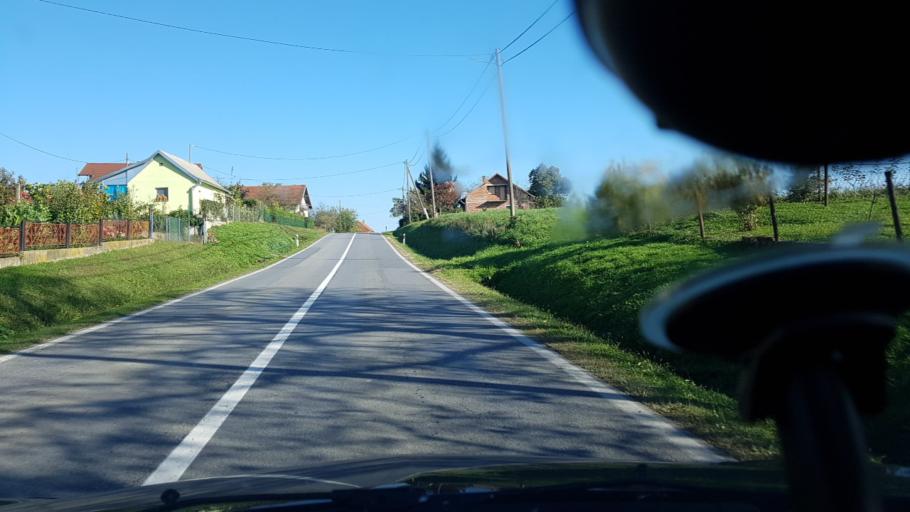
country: HR
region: Bjelovarsko-Bilogorska
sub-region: Grad Cazma
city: Cazma
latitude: 45.7834
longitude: 16.6602
